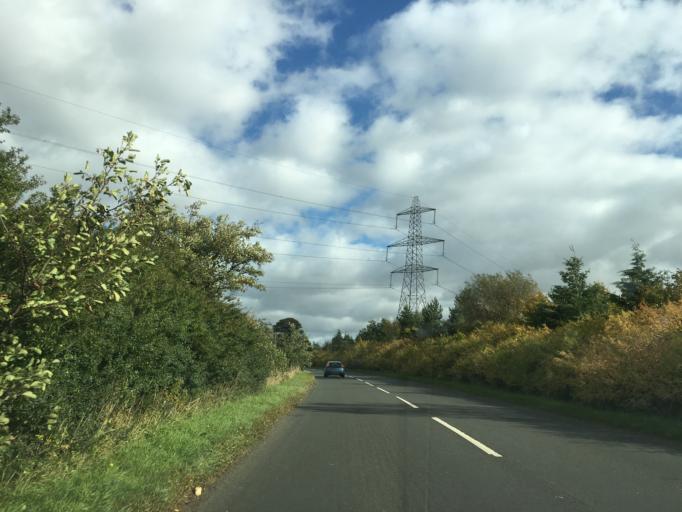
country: GB
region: Scotland
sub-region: East Lothian
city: Ormiston
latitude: 55.8955
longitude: -2.9585
